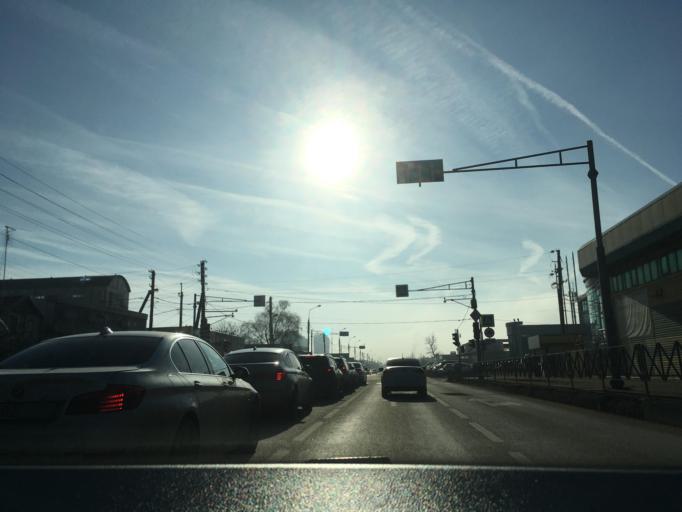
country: RU
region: Krasnodarskiy
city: Krasnodar
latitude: 45.1146
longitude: 39.0119
